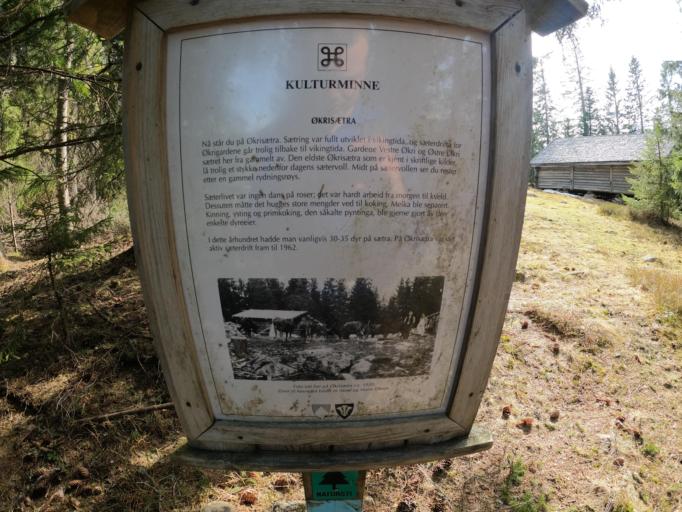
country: NO
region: Akershus
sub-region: Nannestad
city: Teigebyen
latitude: 60.2495
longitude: 10.8898
